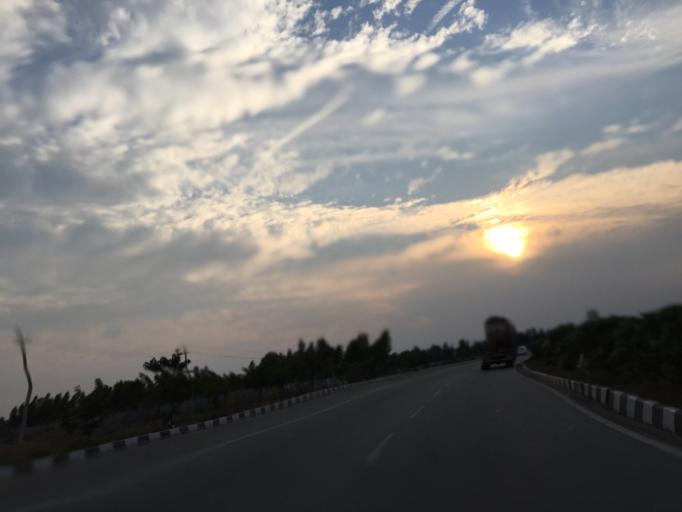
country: IN
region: Karnataka
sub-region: Kolar
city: Kolar
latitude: 13.1281
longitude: 78.0004
